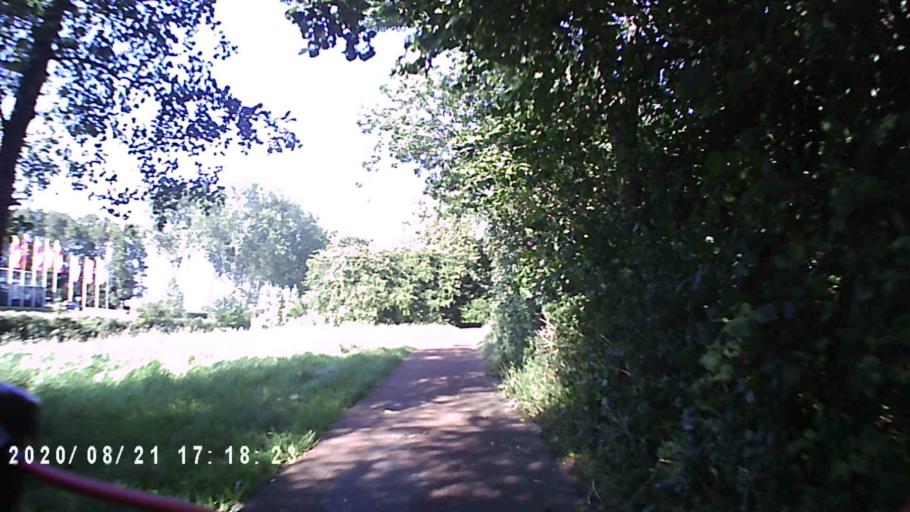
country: NL
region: Groningen
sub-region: Gemeente Groningen
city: Korrewegwijk
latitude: 53.2506
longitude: 6.5820
